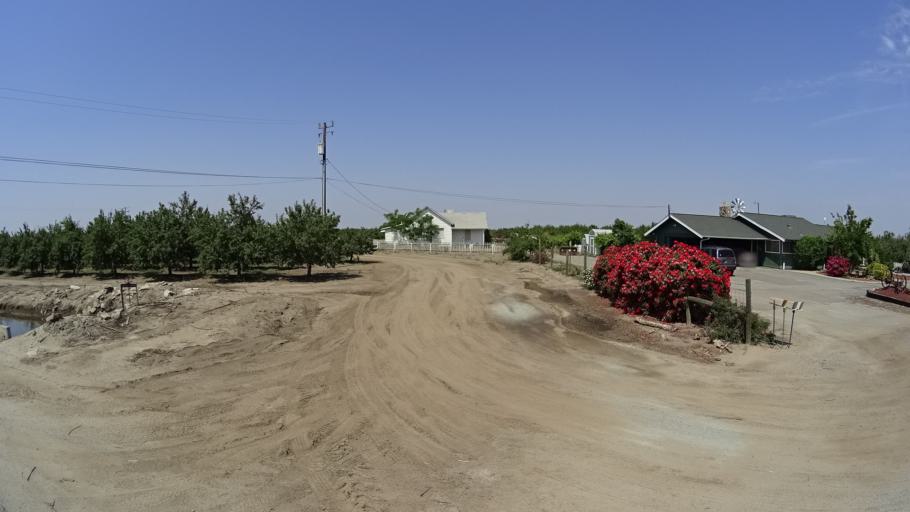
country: US
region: California
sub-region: Kings County
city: Armona
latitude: 36.3244
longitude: -119.7449
